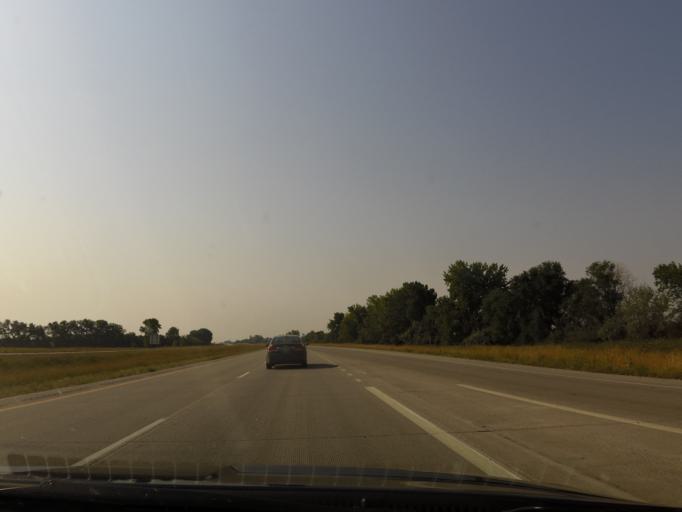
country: US
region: North Dakota
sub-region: Grand Forks County
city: Grand Forks
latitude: 47.6694
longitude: -97.0800
